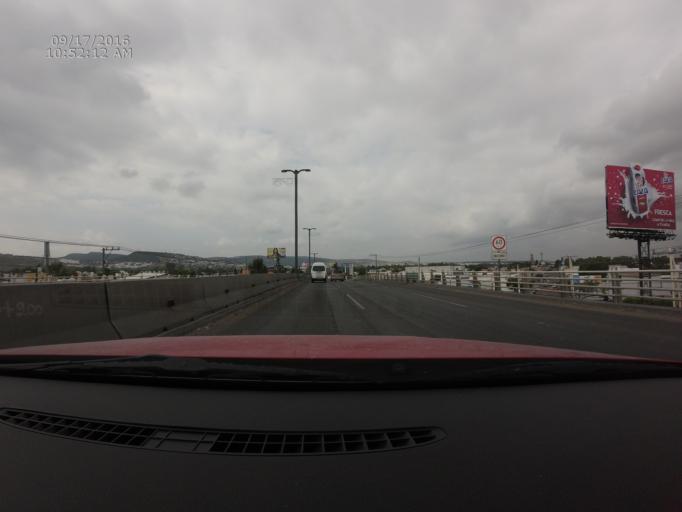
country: MX
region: Queretaro
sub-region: Corregidora
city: El Pueblito
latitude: 20.5412
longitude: -100.4318
